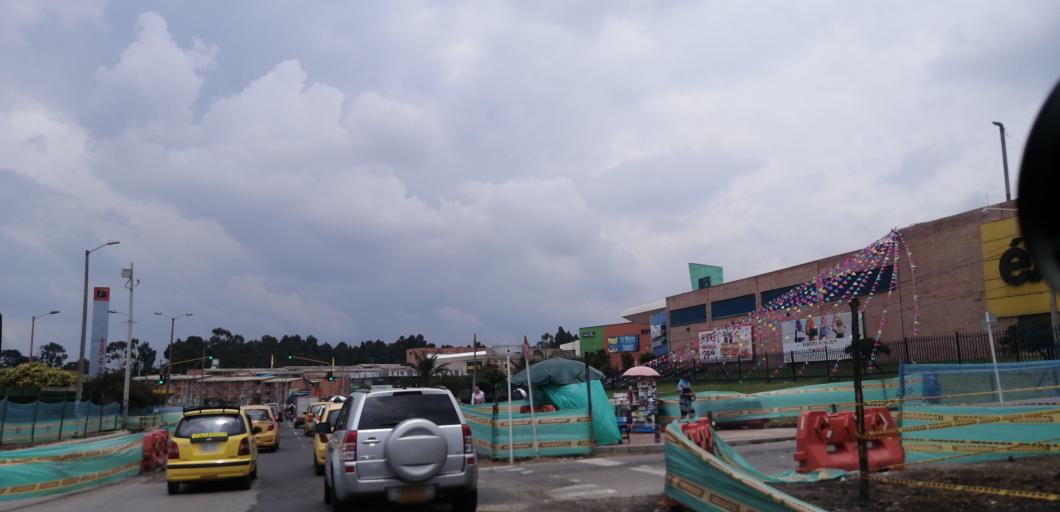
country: CO
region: Bogota D.C.
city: Bogota
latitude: 4.5310
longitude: -74.1189
